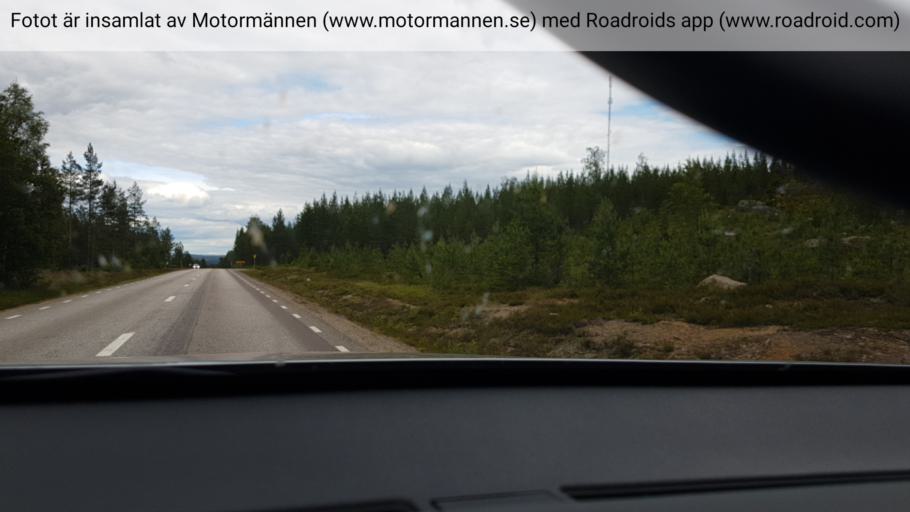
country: NO
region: Hedmark
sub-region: Trysil
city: Innbygda
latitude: 61.0231
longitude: 12.5010
